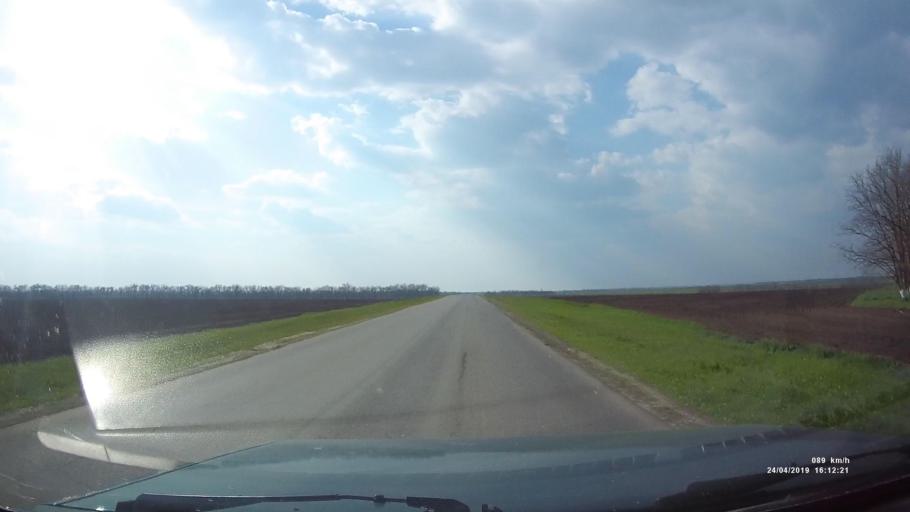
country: RU
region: Rostov
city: Sovetskoye
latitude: 46.7321
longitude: 42.2384
